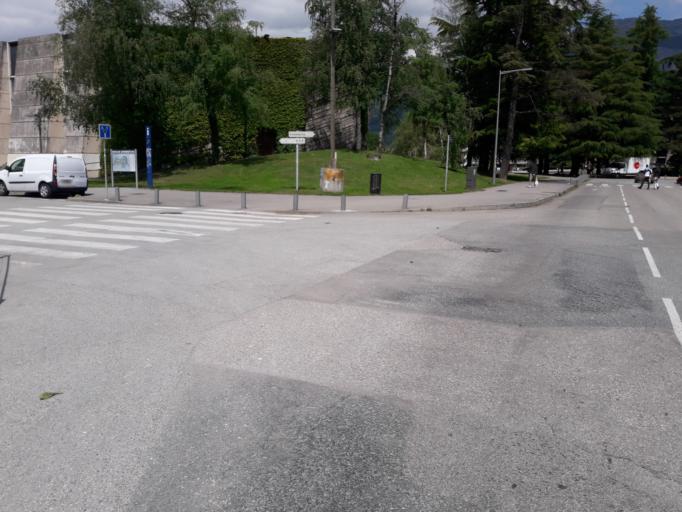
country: FR
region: Rhone-Alpes
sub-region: Departement de l'Isere
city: Corenc
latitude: 45.1908
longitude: 5.7691
